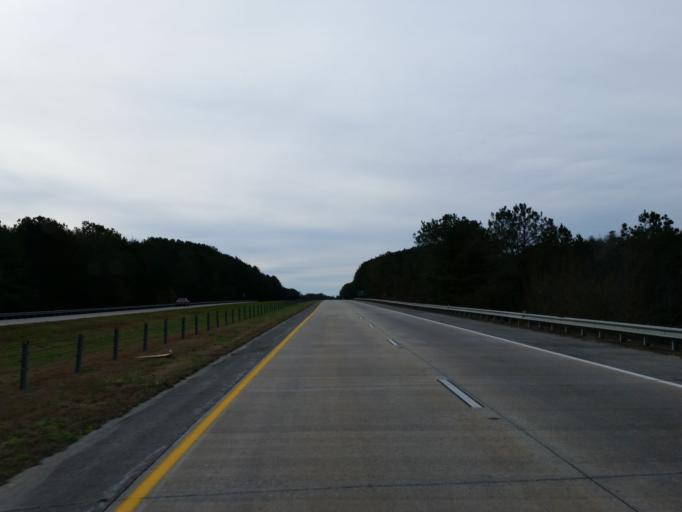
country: US
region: Georgia
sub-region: Cherokee County
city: Ball Ground
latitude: 34.3374
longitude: -84.3924
